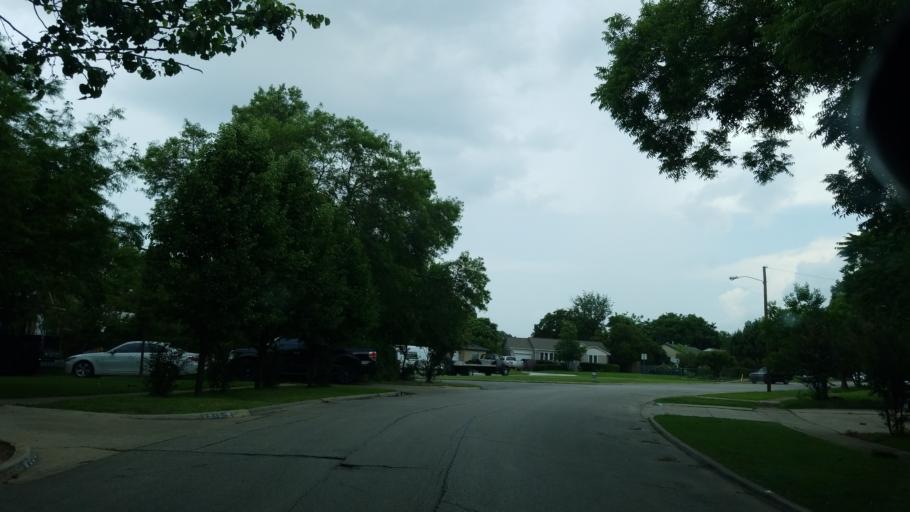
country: US
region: Texas
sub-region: Dallas County
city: Farmers Branch
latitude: 32.8784
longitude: -96.8628
